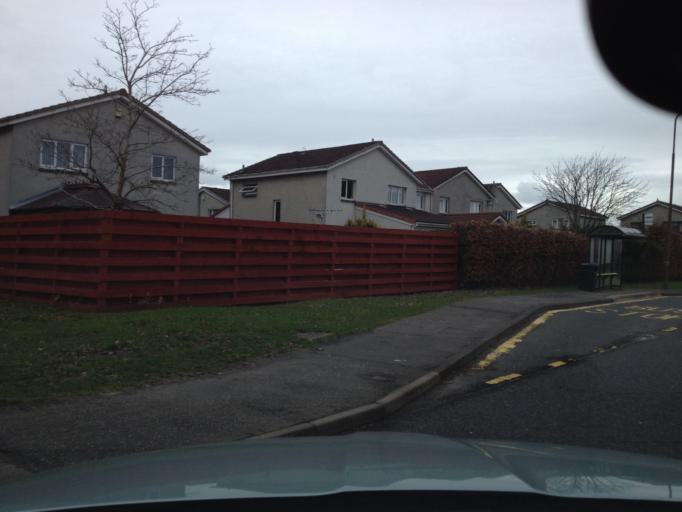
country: GB
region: Scotland
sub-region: West Lothian
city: Mid Calder
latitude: 55.8862
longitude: -3.4928
